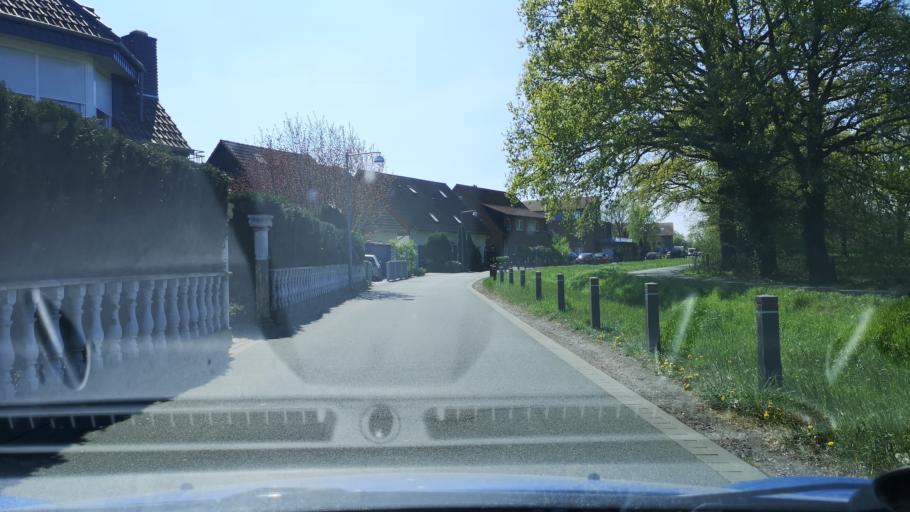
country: DE
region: Lower Saxony
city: Langenhagen
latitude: 52.4834
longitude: 9.7296
